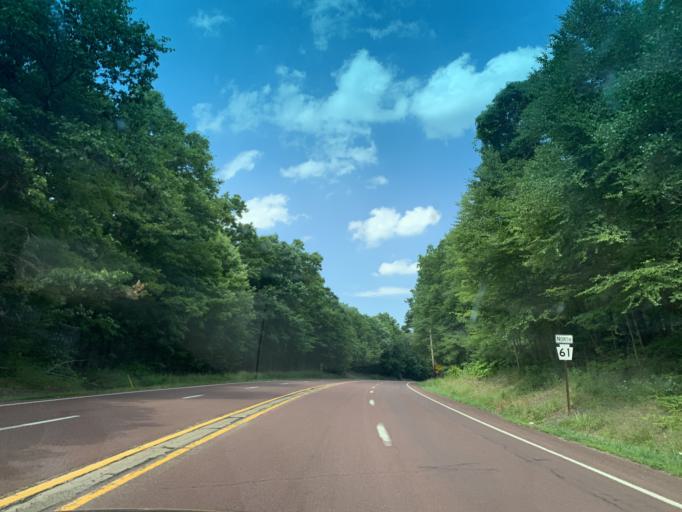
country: US
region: Pennsylvania
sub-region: Schuylkill County
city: Ashland
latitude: 40.7857
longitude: -76.3558
